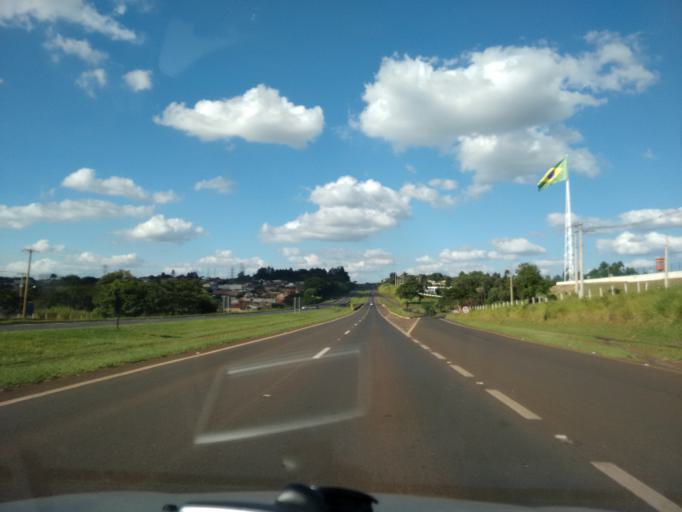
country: BR
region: Sao Paulo
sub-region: Araraquara
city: Araraquara
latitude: -21.8160
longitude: -48.1731
